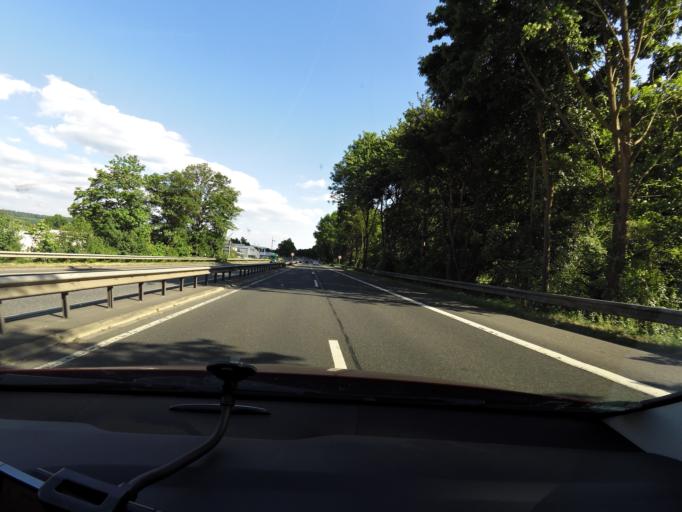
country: DE
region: Rheinland-Pfalz
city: Sinzig
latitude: 50.5320
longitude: 7.2716
